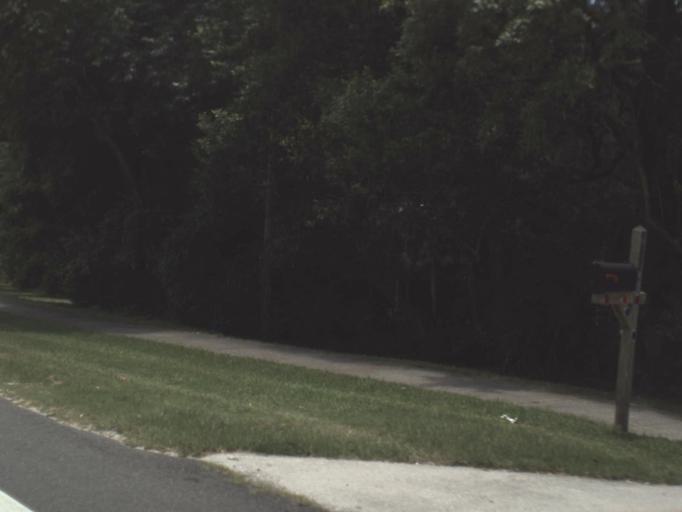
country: US
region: Florida
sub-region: Clay County
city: Keystone Heights
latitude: 29.7796
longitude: -82.0214
